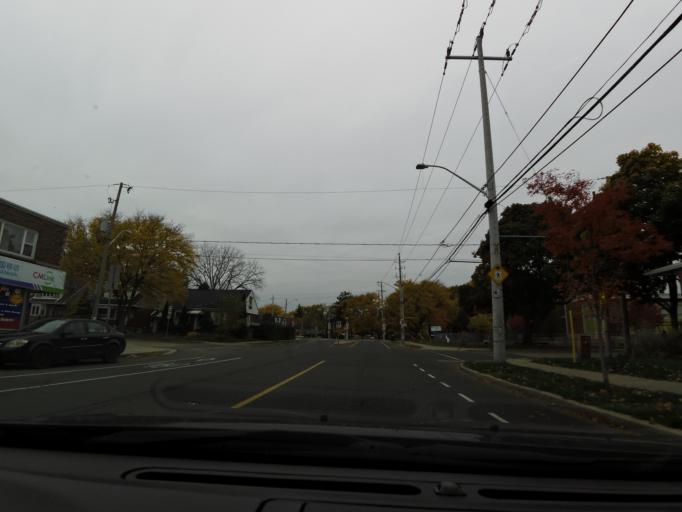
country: CA
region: Ontario
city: Hamilton
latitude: 43.2632
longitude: -79.9013
